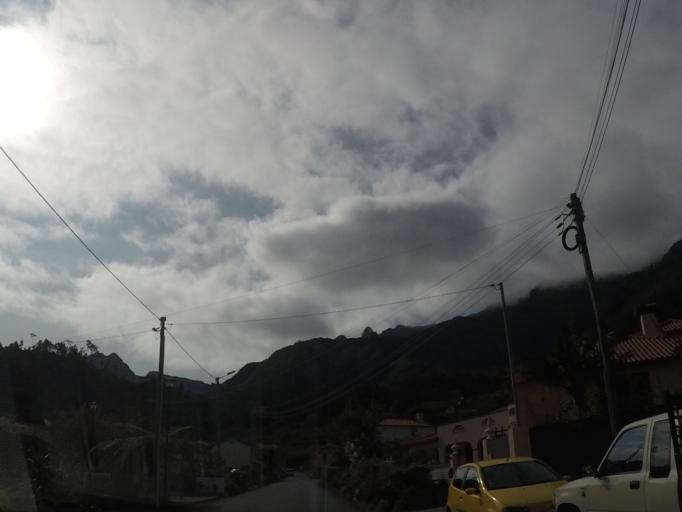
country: PT
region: Madeira
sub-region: Sao Vicente
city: Sao Vicente
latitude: 32.7829
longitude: -17.0438
